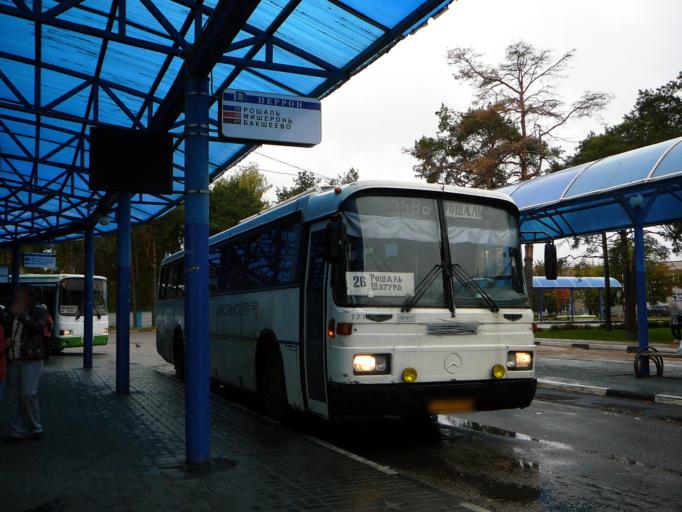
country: RU
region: Moskovskaya
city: Shatura
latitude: 55.5747
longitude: 39.5256
